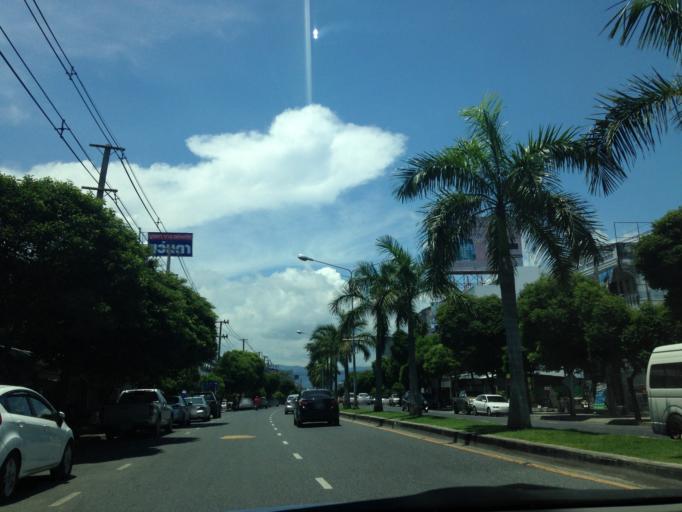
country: TH
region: Chon Buri
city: Chon Buri
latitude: 13.2868
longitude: 100.9284
